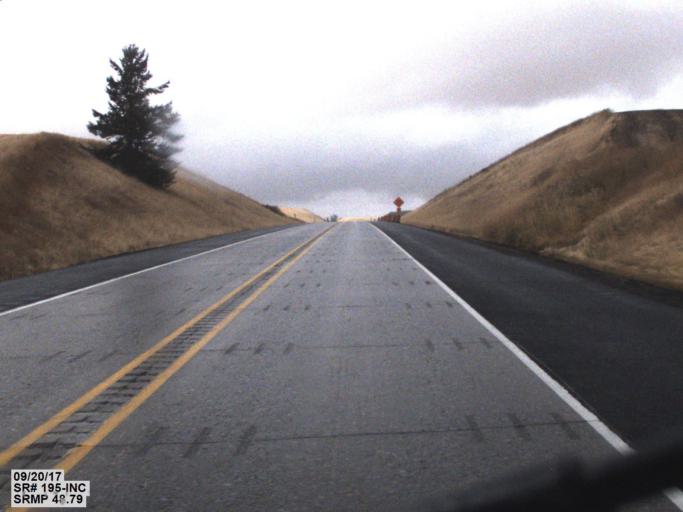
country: US
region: Washington
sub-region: Whitman County
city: Colfax
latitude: 47.0174
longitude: -117.3564
